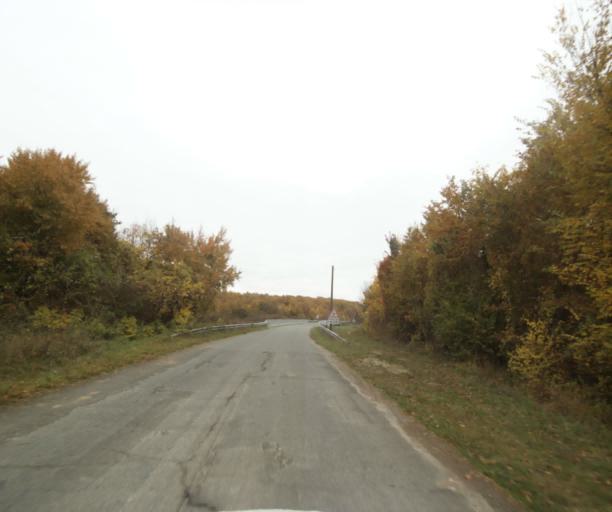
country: FR
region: Poitou-Charentes
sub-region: Departement de la Charente-Maritime
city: Chermignac
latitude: 45.7147
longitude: -0.6629
